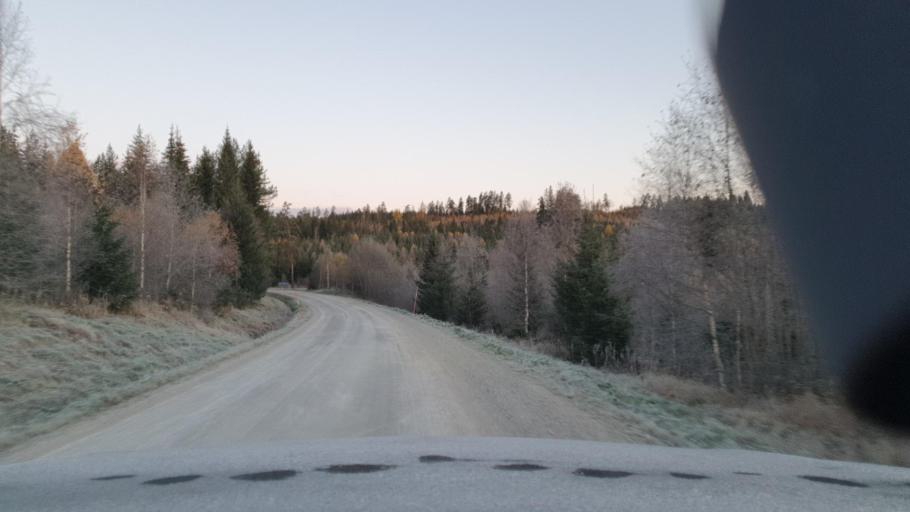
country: SE
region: Vaermland
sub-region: Arvika Kommun
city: Arvika
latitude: 59.8365
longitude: 12.7466
